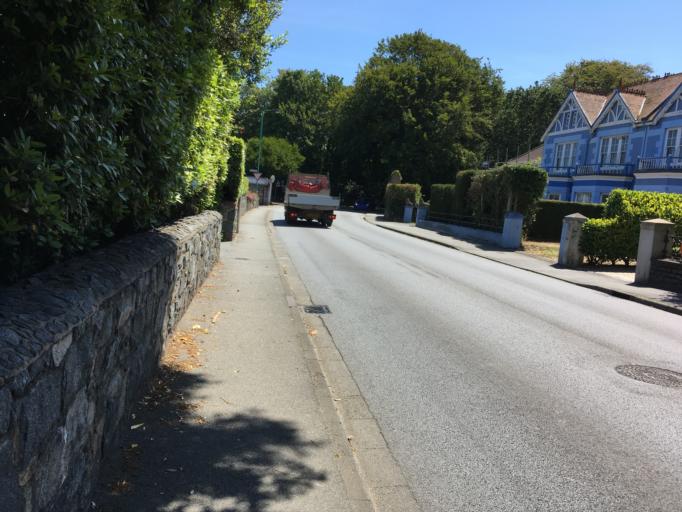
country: GG
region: St Peter Port
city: Saint Peter Port
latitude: 49.4590
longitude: -2.5539
